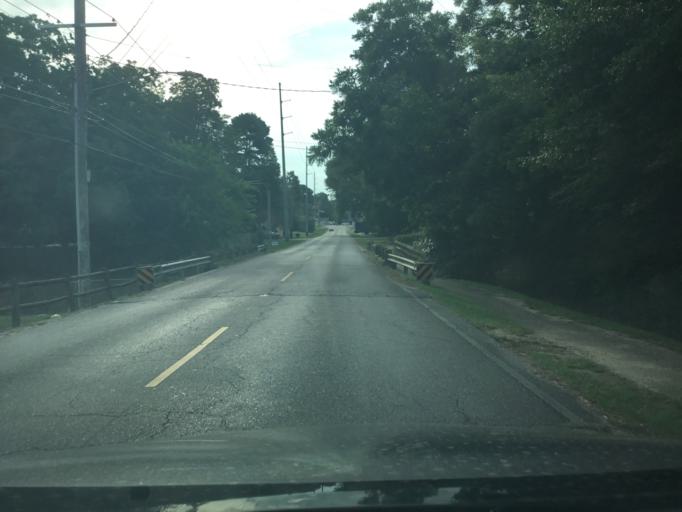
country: US
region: Alabama
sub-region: Montgomery County
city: Montgomery
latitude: 32.3671
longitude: -86.2481
